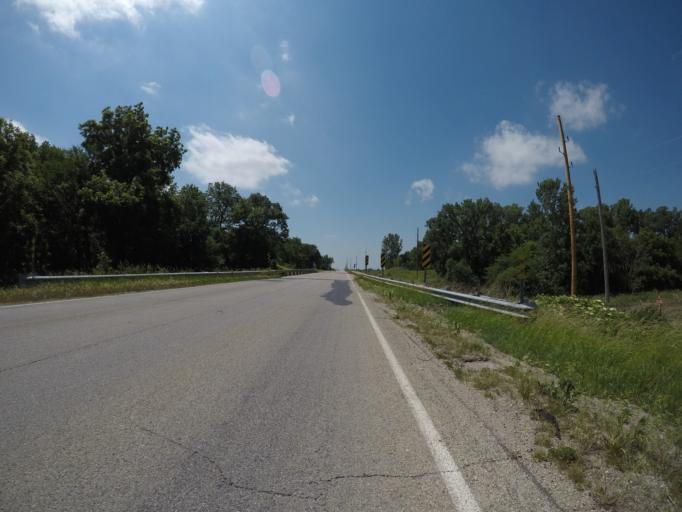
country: US
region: Kansas
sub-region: Pottawatomie County
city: Westmoreland
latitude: 39.3415
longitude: -96.4360
